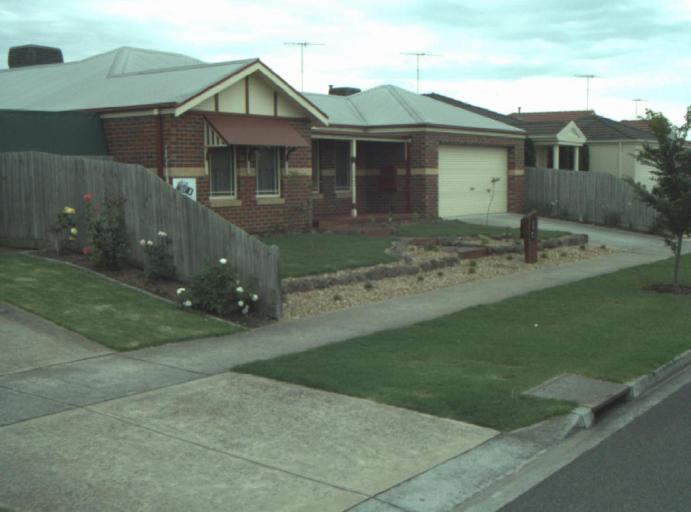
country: AU
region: Victoria
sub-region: Greater Geelong
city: Breakwater
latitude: -38.1922
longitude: 144.3931
